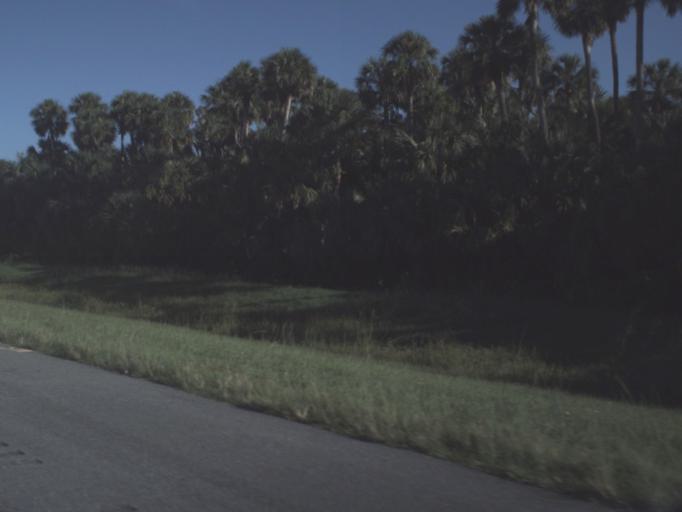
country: US
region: Florida
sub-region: Seminole County
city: Oviedo
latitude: 28.7236
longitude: -81.2453
